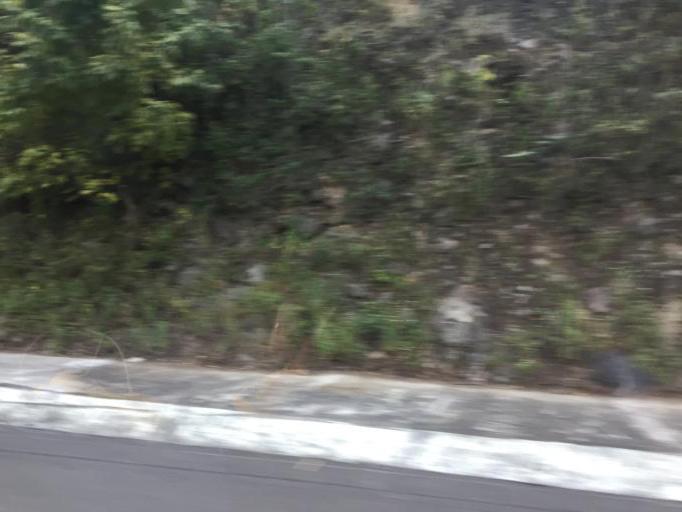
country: MX
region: Michoacan
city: Panindicuaro de la Reforma
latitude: 19.9746
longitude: -101.7442
